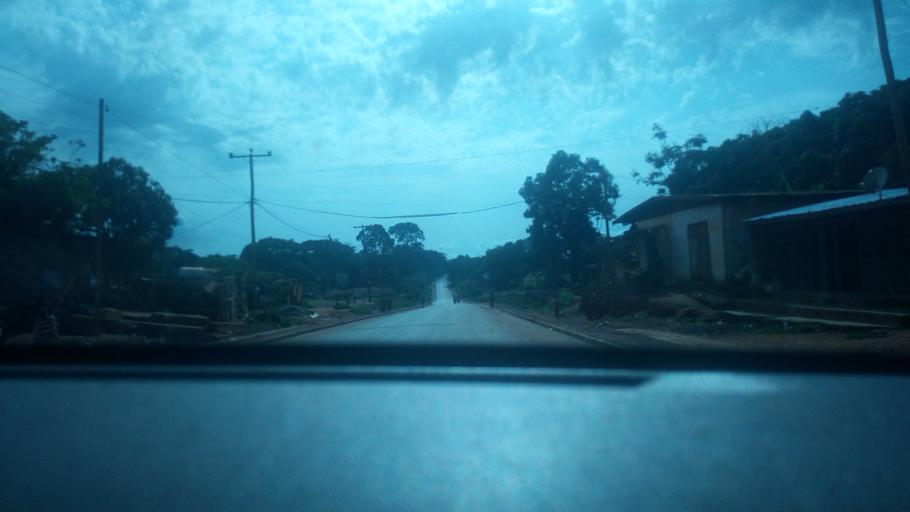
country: CM
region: Centre
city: Nkoteng
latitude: 4.5049
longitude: 12.1182
